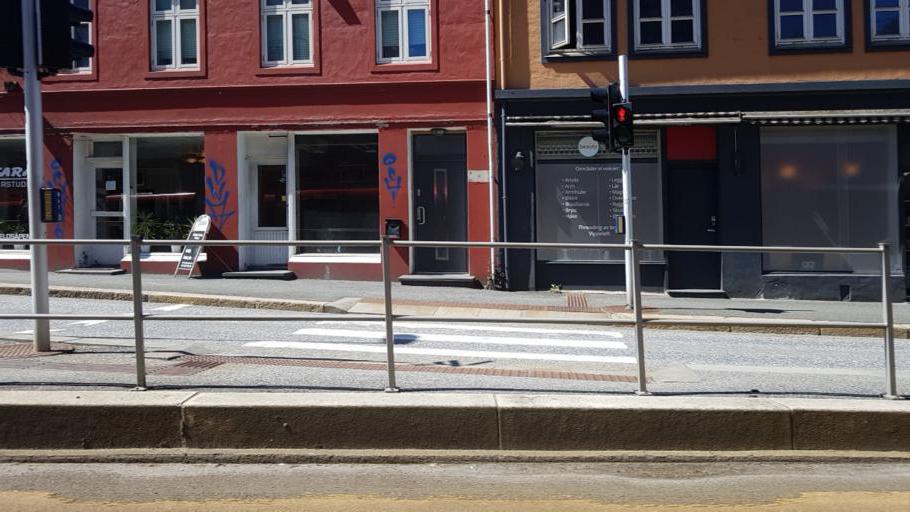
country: NO
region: Hordaland
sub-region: Bergen
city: Bergen
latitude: 60.3613
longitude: 5.3509
